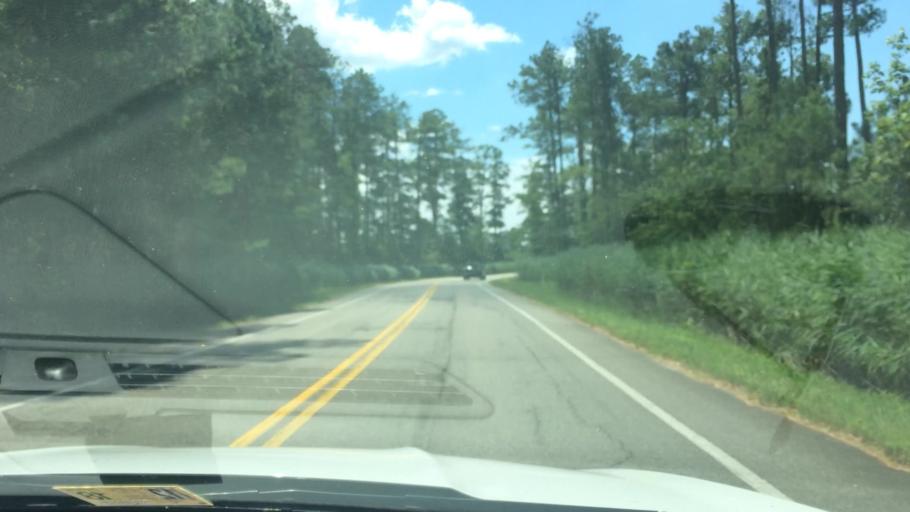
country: US
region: Virginia
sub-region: King William County
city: West Point
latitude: 37.5471
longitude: -76.7934
